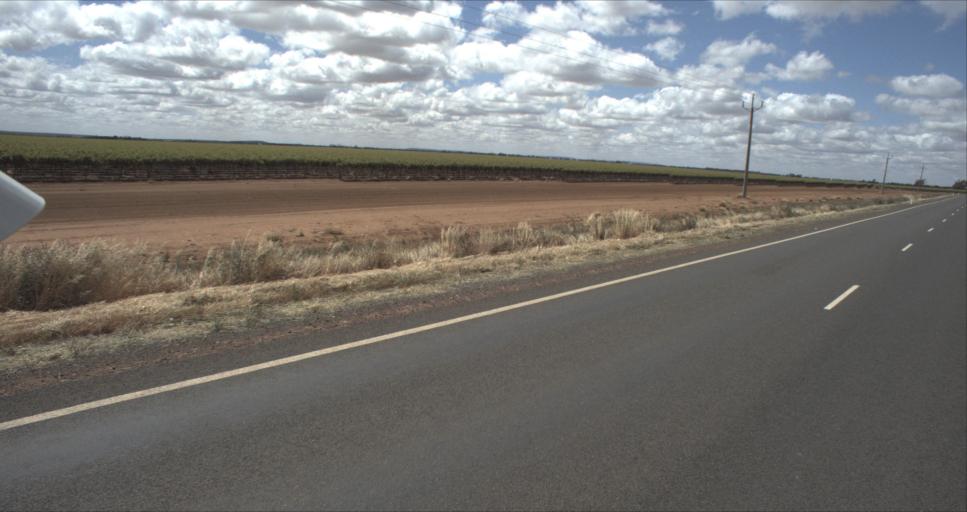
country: AU
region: New South Wales
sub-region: Murrumbidgee Shire
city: Darlington Point
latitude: -34.4739
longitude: 146.1459
